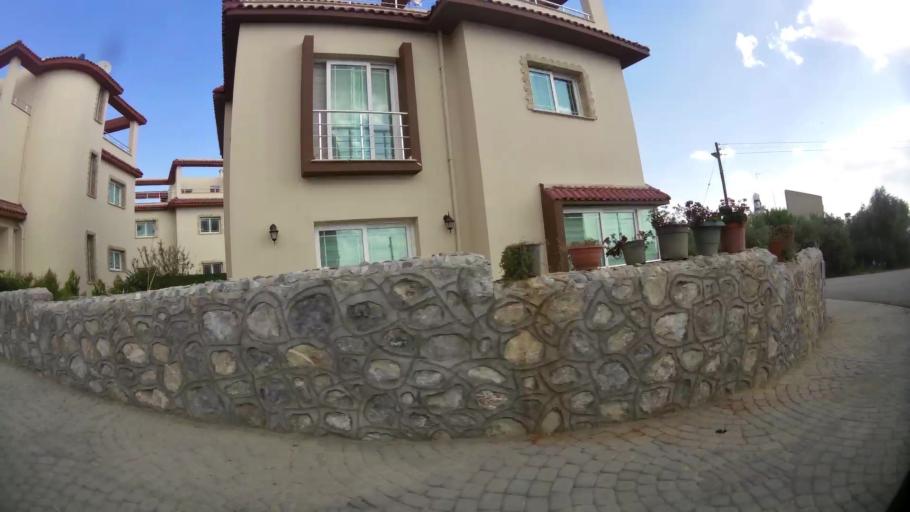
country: CY
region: Lefkosia
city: Nicosia
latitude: 35.2243
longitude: 33.3738
